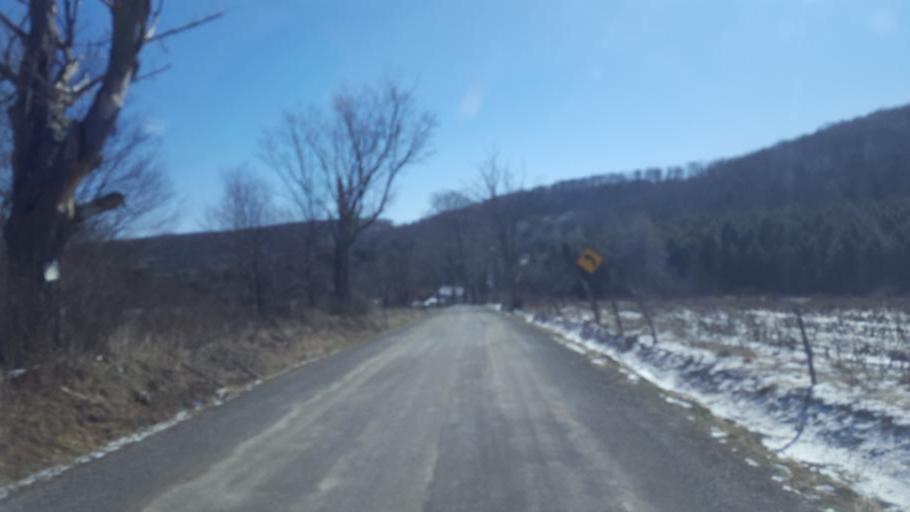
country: US
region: New York
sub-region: Allegany County
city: Wellsville
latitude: 42.0490
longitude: -77.9719
